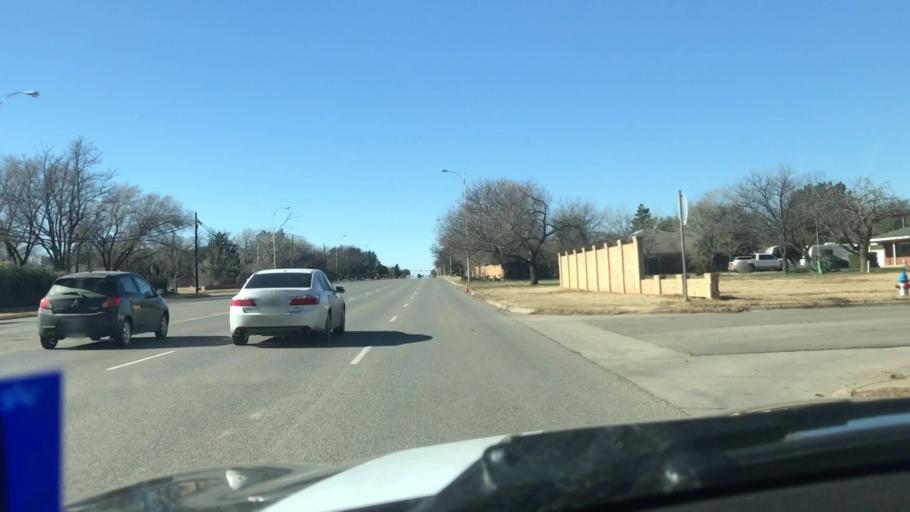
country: US
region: Texas
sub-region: Lubbock County
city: Lubbock
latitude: 33.5779
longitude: -101.9239
